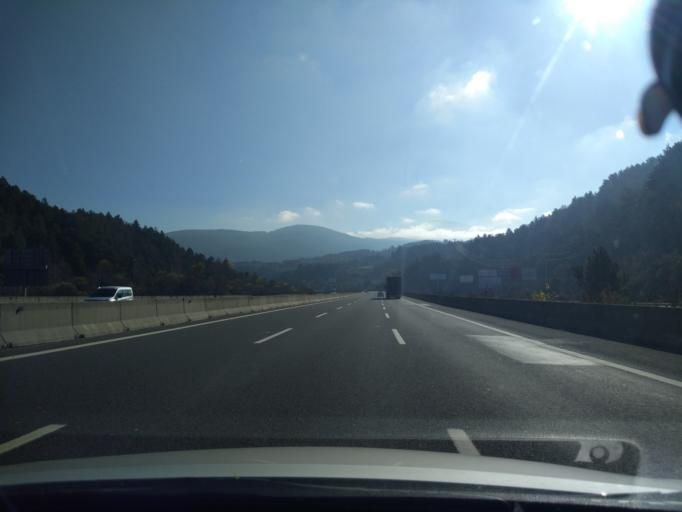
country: TR
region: Bolu
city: Bolu
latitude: 40.7464
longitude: 31.7814
